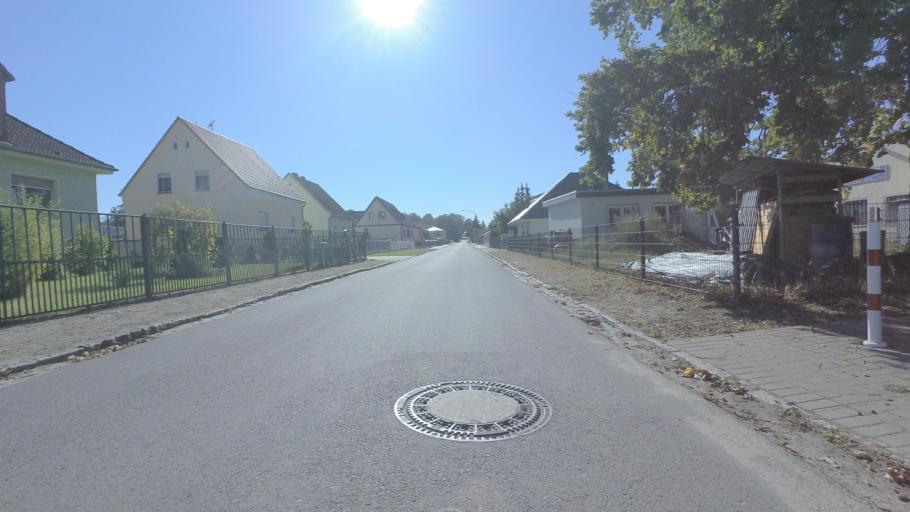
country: DE
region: Brandenburg
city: Sperenberg
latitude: 52.1473
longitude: 13.3682
